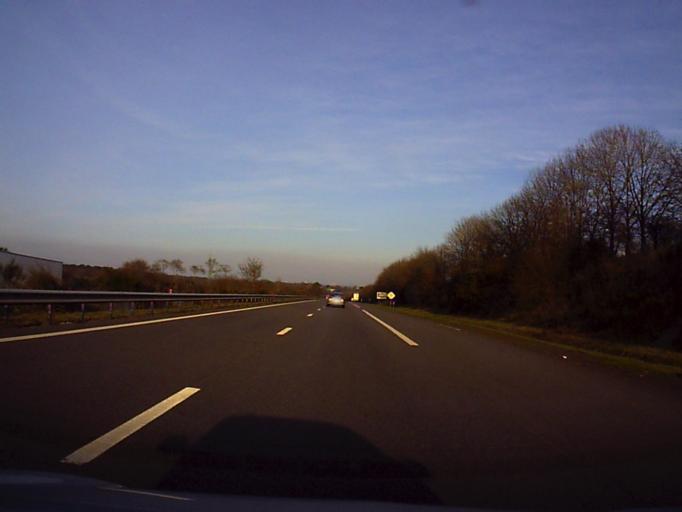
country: FR
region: Brittany
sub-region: Departement d'Ille-et-Vilaine
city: Saint-Thurial
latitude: 48.0404
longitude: -1.9528
